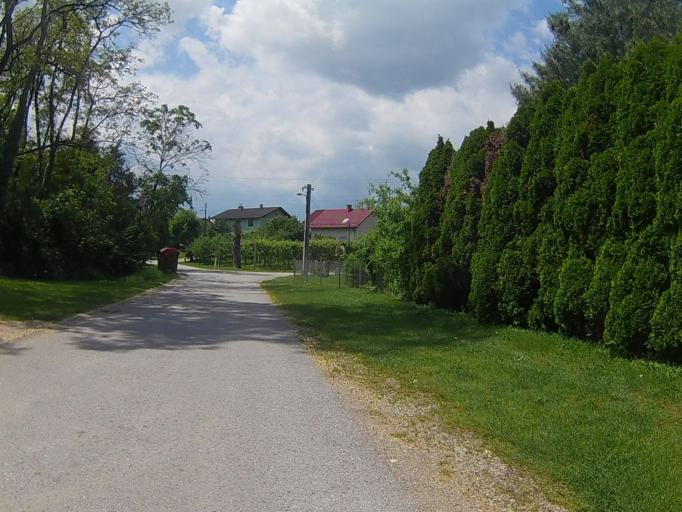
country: SI
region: Miklavz na Dravskem Polju
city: Miklavz na Dravskem Polju
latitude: 46.5201
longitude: 15.7035
